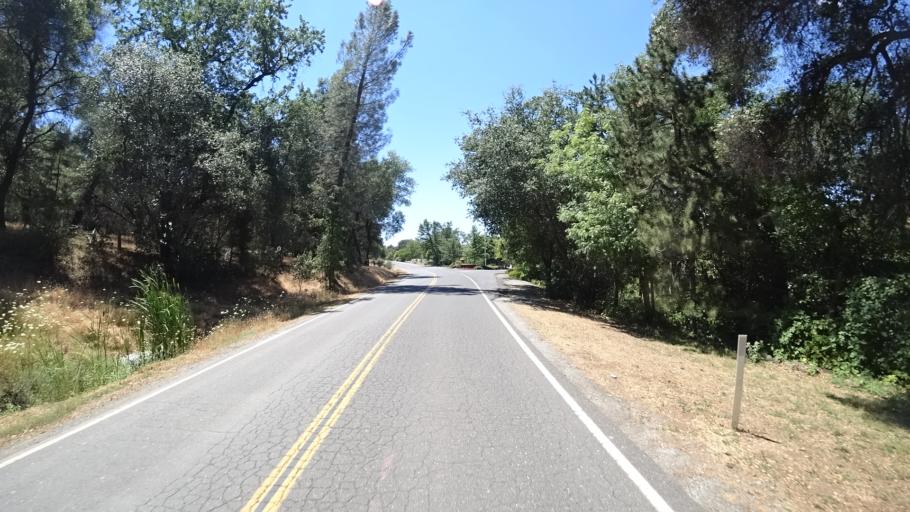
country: US
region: California
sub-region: Calaveras County
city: Murphys
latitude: 38.1214
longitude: -120.4662
